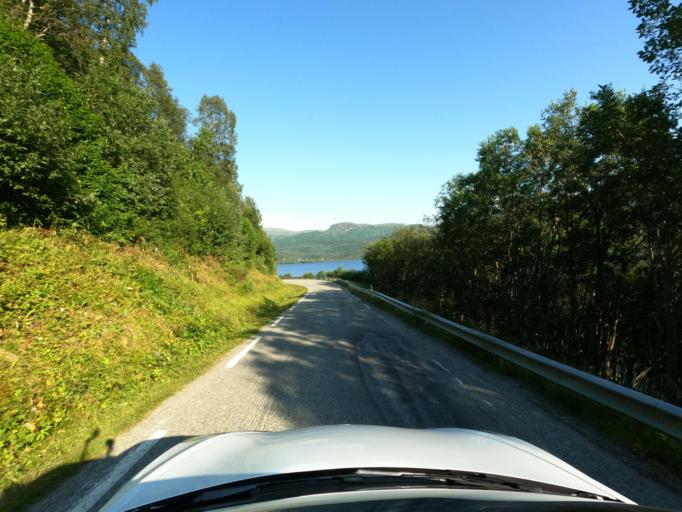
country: NO
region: Troms
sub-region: Gratangen
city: Gratangen
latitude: 68.5597
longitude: 17.6671
